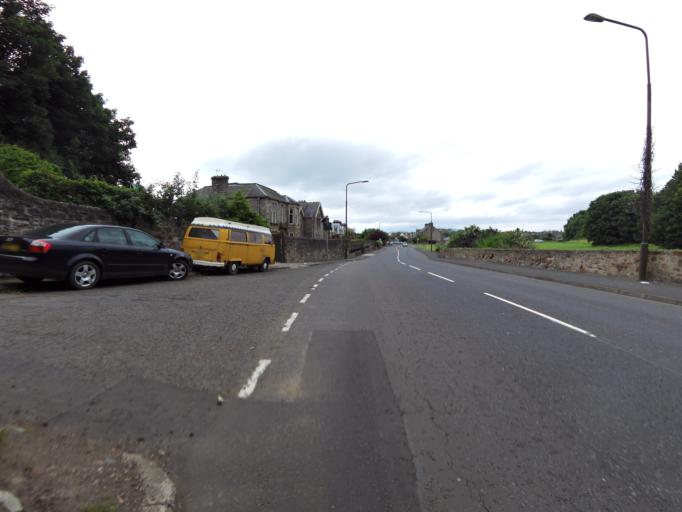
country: GB
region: Scotland
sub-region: East Lothian
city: Musselburgh
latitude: 55.9468
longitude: -3.0213
